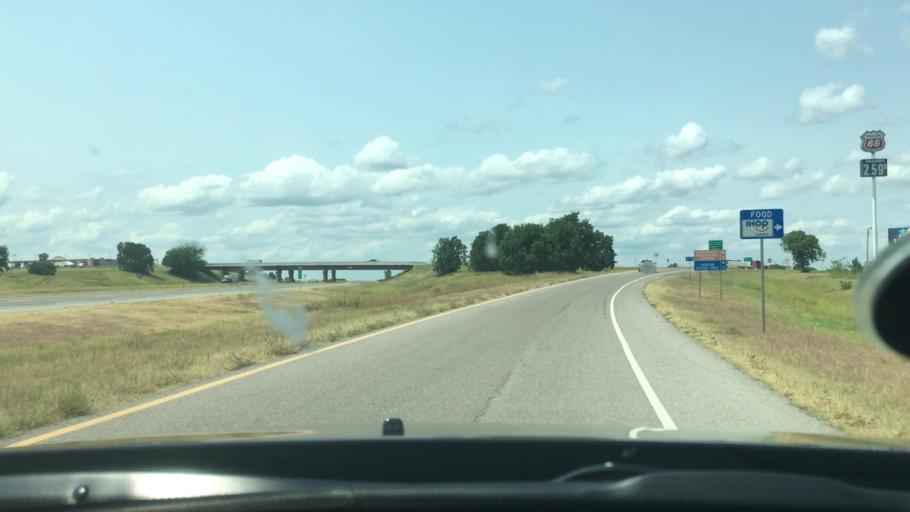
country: US
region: Oklahoma
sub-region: Murray County
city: Davis
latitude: 34.5038
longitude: -97.1720
